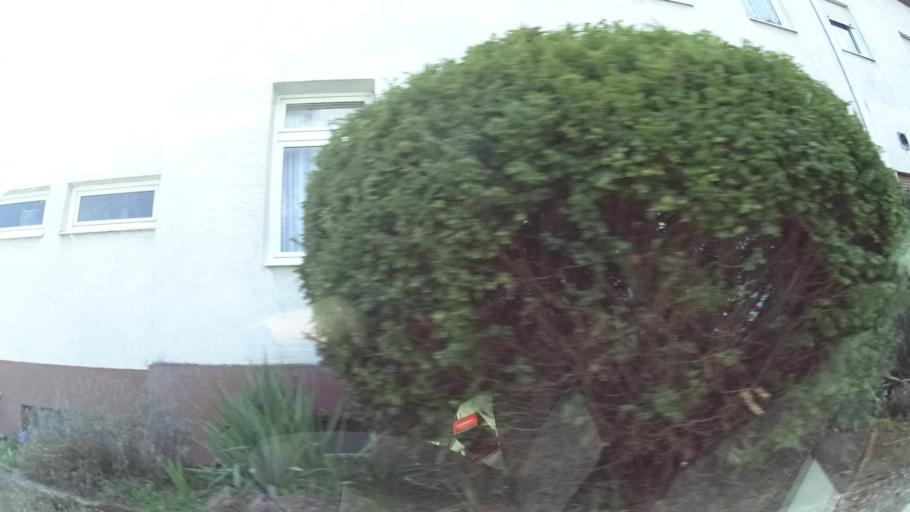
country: DE
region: Rheinland-Pfalz
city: Kirschweiler
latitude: 49.7566
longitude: 7.2426
